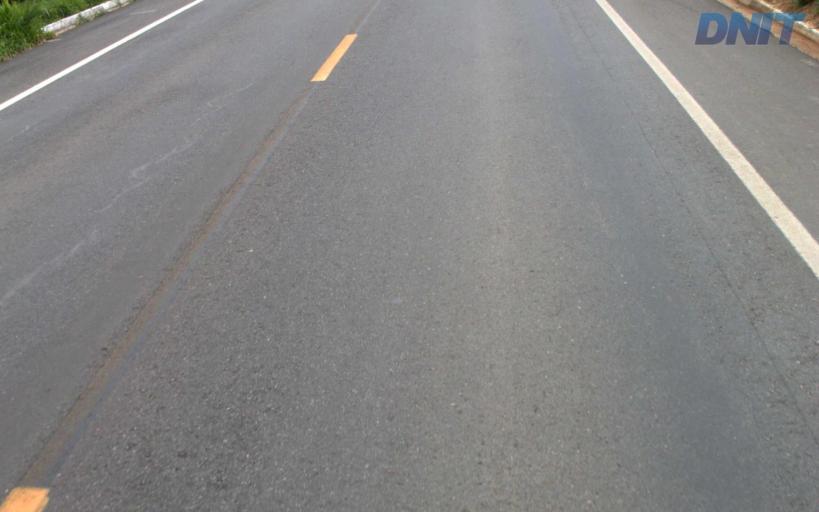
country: BR
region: Minas Gerais
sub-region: Governador Valadares
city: Governador Valadares
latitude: -18.9344
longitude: -42.0502
